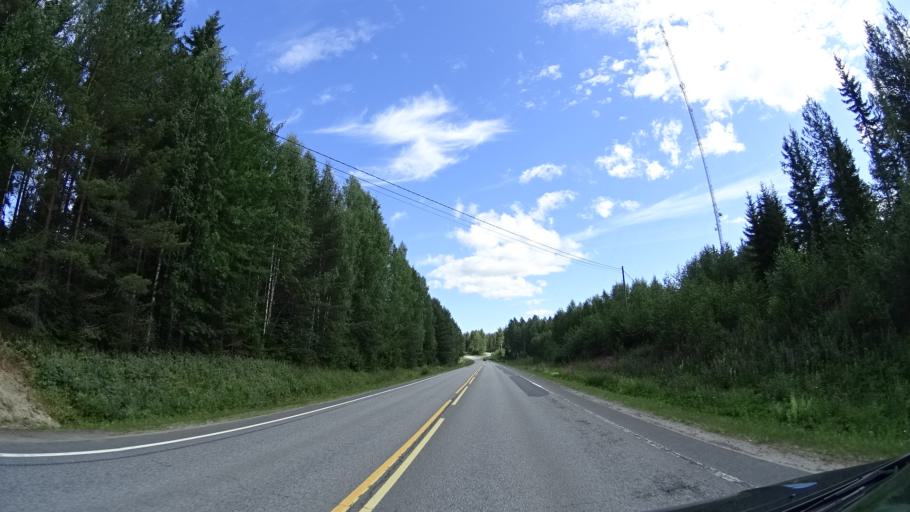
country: FI
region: Pirkanmaa
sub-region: Luoteis-Pirkanmaa
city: Kihnioe
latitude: 62.1510
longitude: 23.1587
